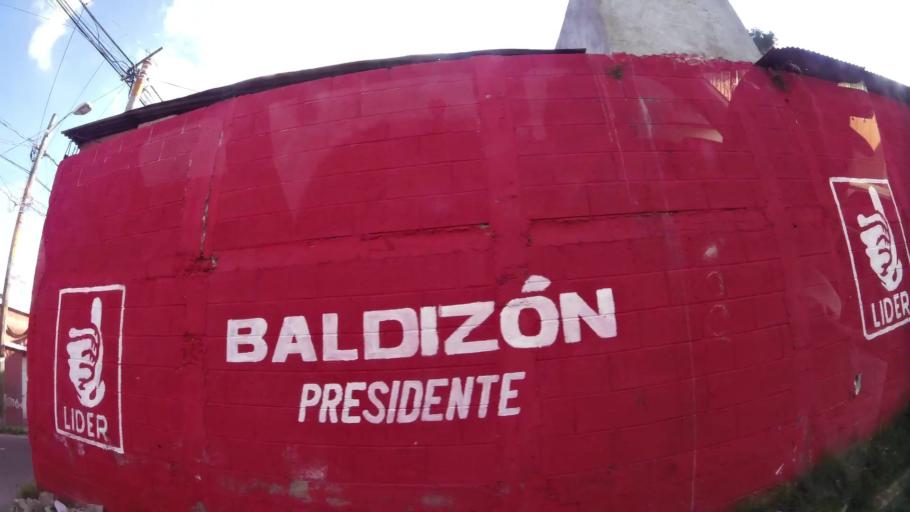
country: GT
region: Guatemala
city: Villa Nueva
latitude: 14.5238
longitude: -90.5785
